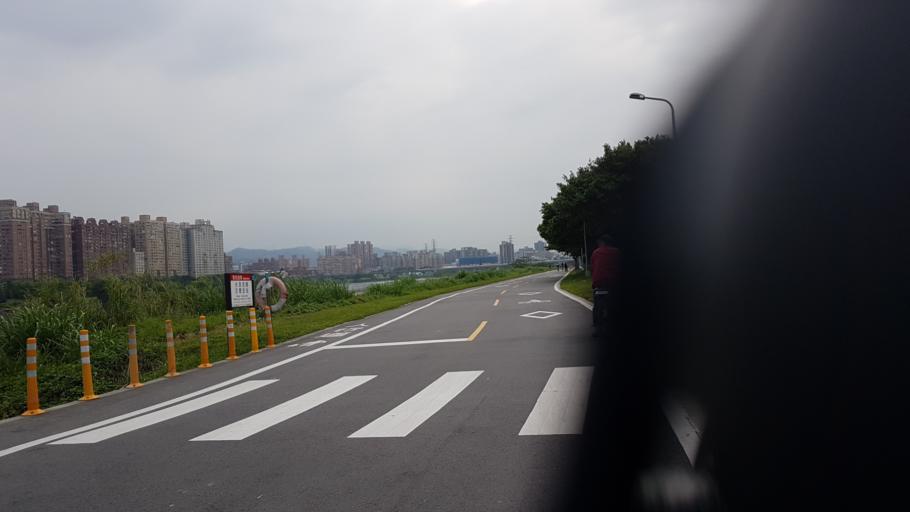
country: TW
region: Taipei
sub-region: Taipei
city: Banqiao
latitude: 25.0173
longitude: 121.5034
